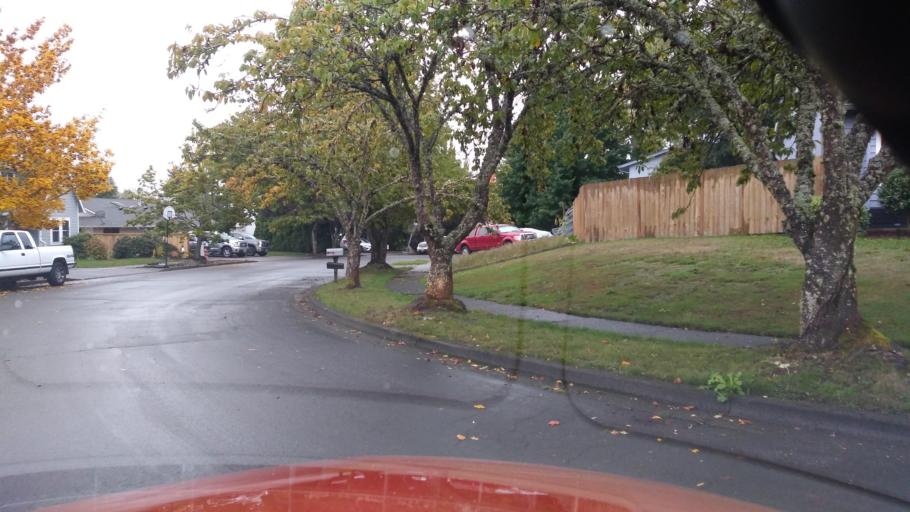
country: US
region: Oregon
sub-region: Washington County
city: Cornelius
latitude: 45.5237
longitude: -123.0336
